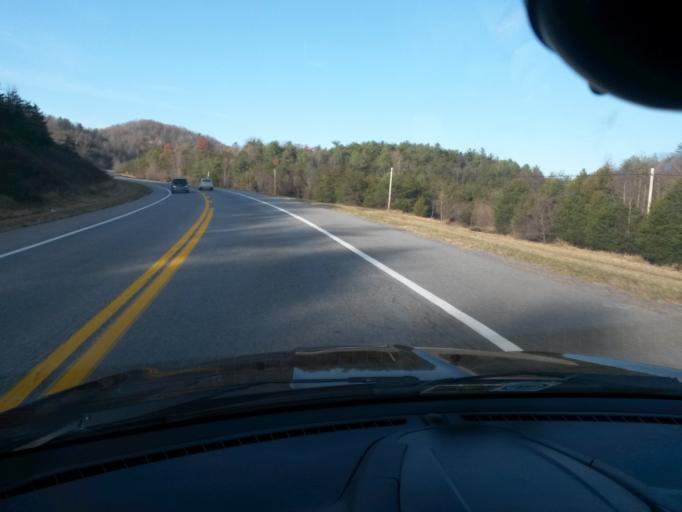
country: US
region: Virginia
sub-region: Alleghany County
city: Clifton Forge
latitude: 37.7536
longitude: -79.7872
